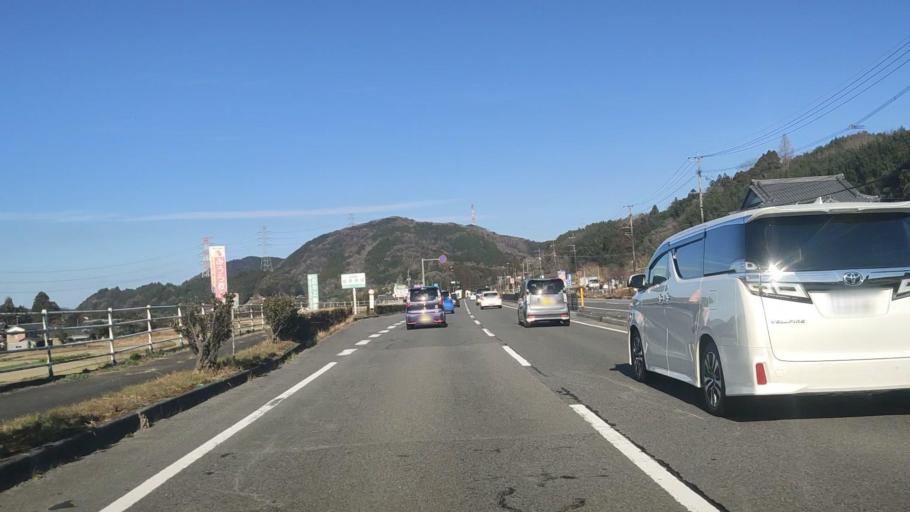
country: JP
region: Oita
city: Oita
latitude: 33.1028
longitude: 131.6524
